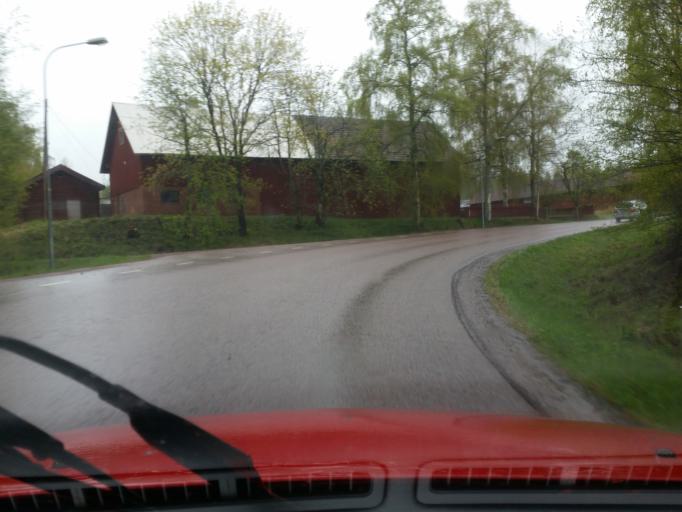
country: SE
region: Dalarna
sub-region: Saters Kommun
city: Saeter
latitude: 60.3456
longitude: 15.7850
